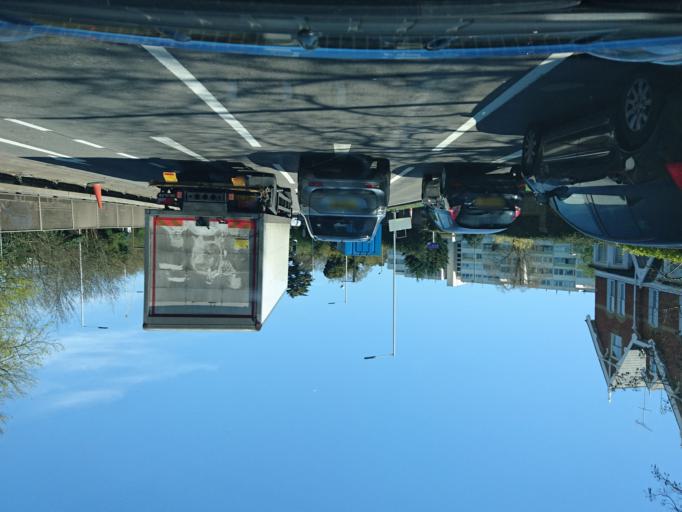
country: GB
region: England
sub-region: Greater London
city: Hendon
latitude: 51.5945
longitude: -0.2157
